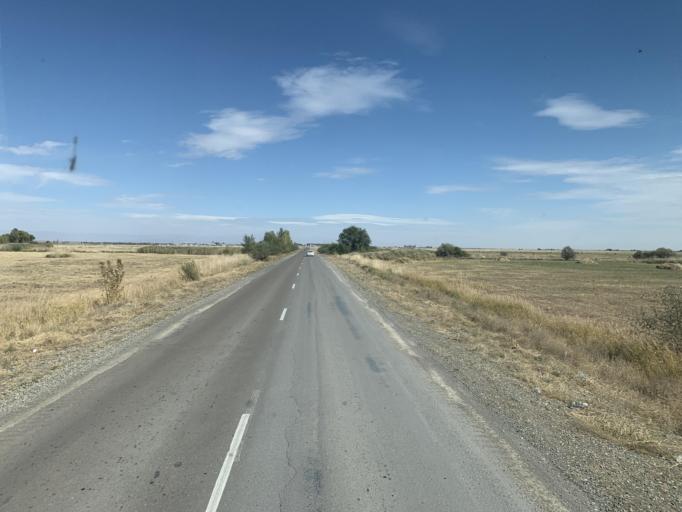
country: CN
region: Xinjiang Uygur Zizhiqu
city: Tacheng
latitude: 46.6638
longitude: 82.7513
